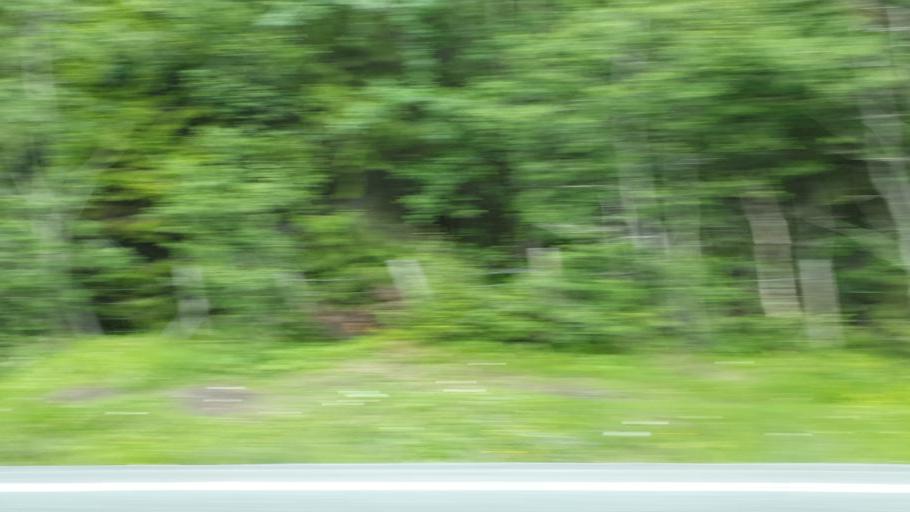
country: NO
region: Sor-Trondelag
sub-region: Rennebu
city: Berkak
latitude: 62.8592
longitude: 10.0211
